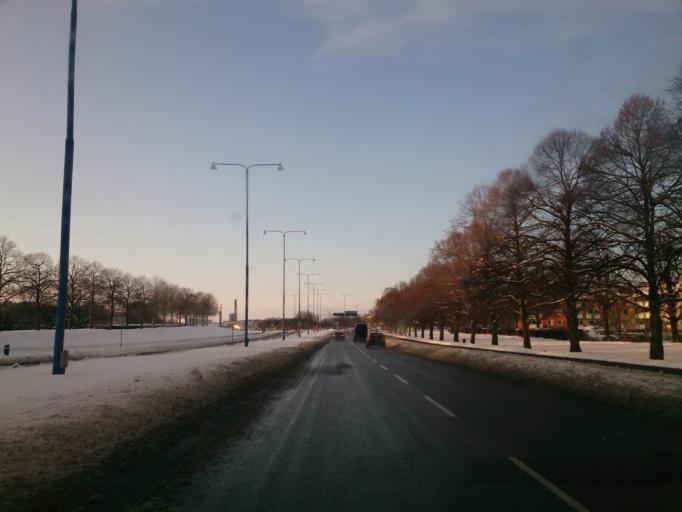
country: SE
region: OEstergoetland
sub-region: Norrkopings Kommun
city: Norrkoping
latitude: 58.5938
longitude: 16.1621
